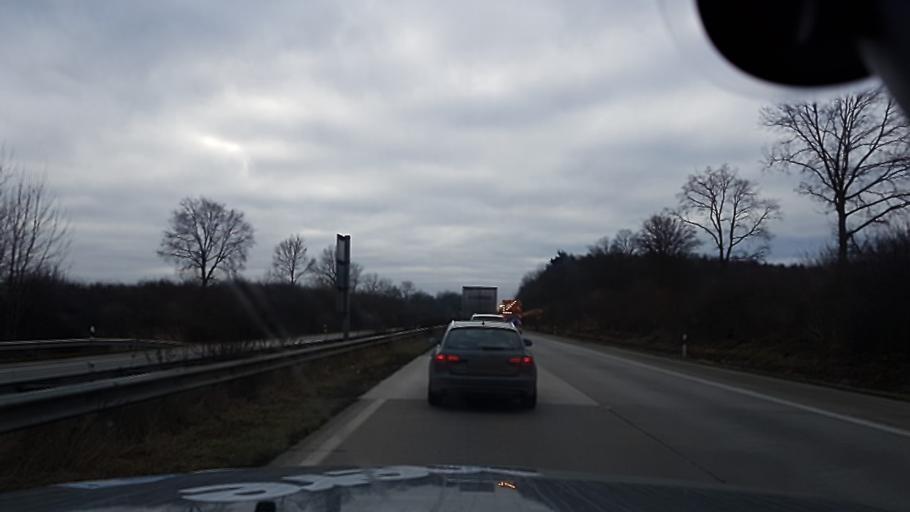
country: DE
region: Schleswig-Holstein
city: Scharbeutz
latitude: 53.9946
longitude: 10.7326
